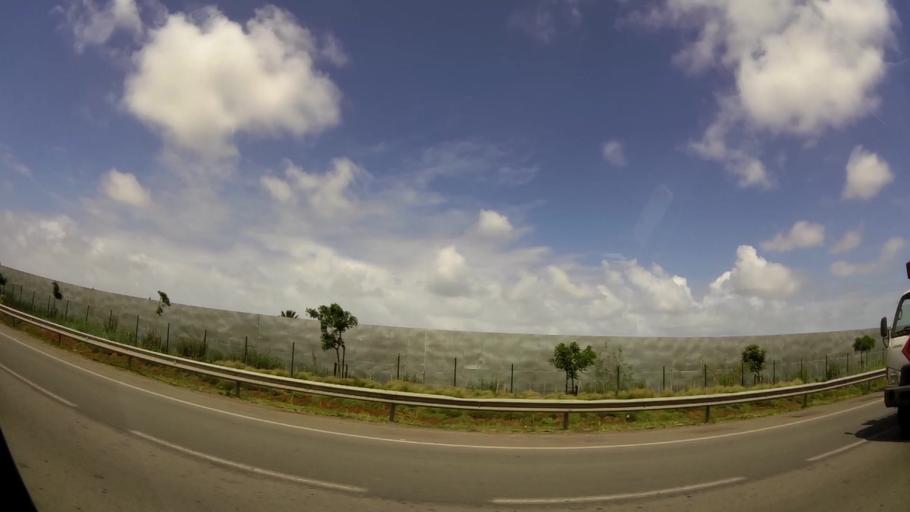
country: MA
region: Grand Casablanca
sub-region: Mediouna
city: Tit Mellil
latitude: 33.6230
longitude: -7.4690
